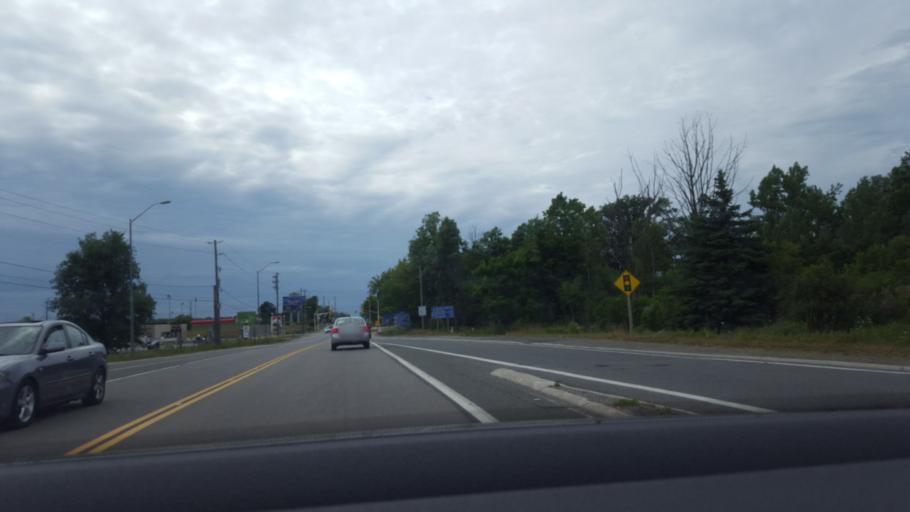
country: CA
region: Ontario
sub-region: Halton
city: Milton
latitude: 43.4926
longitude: -79.9900
